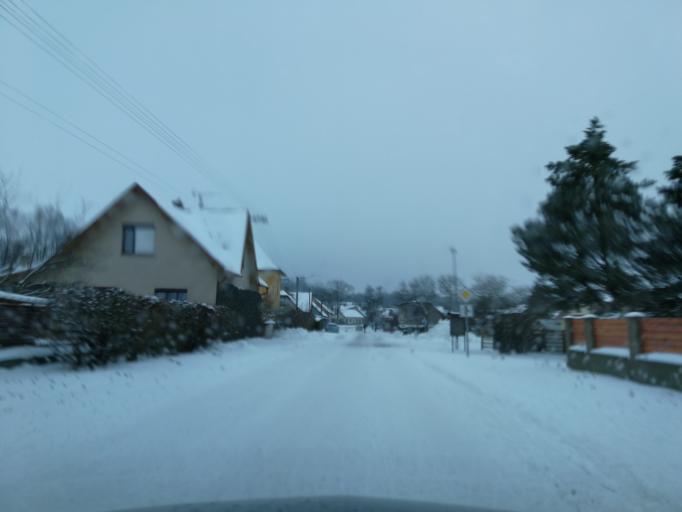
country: CZ
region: Vysocina
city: Heralec
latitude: 49.5293
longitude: 15.4624
